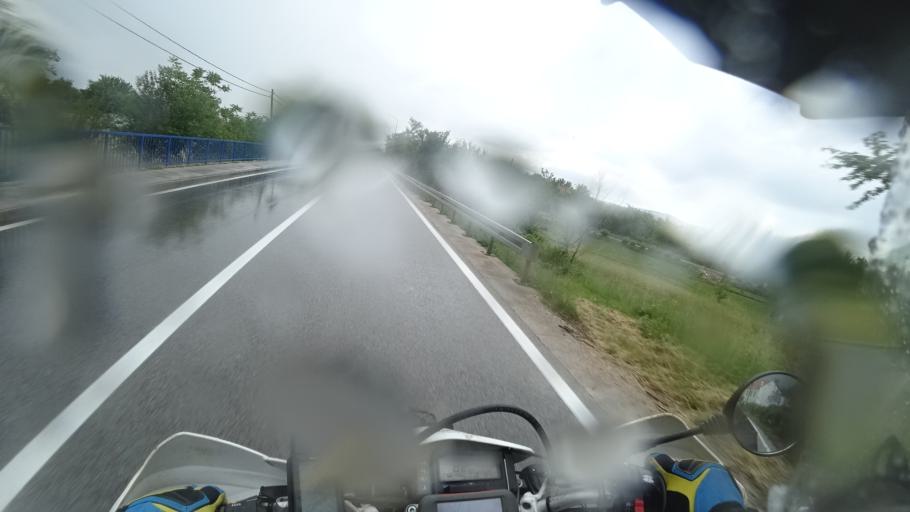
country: HR
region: Sibensko-Kniniska
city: Knin
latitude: 44.0438
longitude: 16.2216
